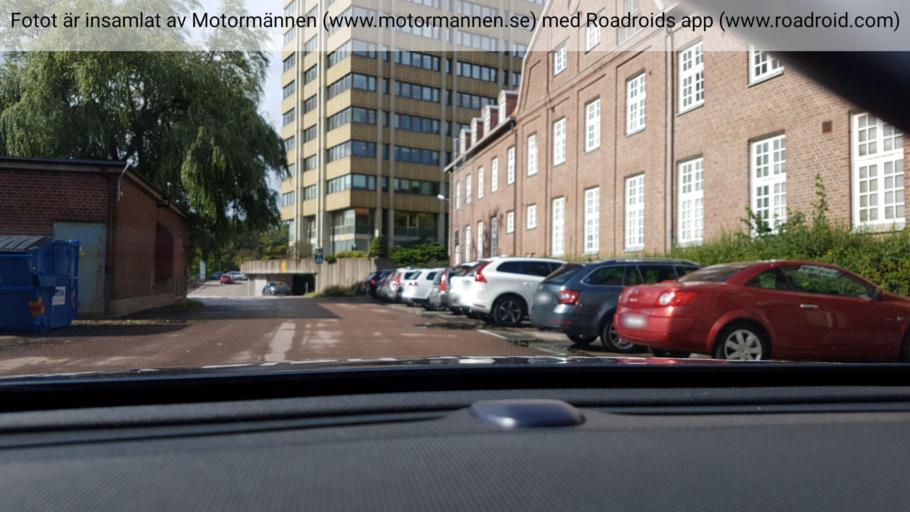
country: SE
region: Vaestra Goetaland
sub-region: Goteborg
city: Eriksbo
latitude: 57.7280
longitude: 12.0144
